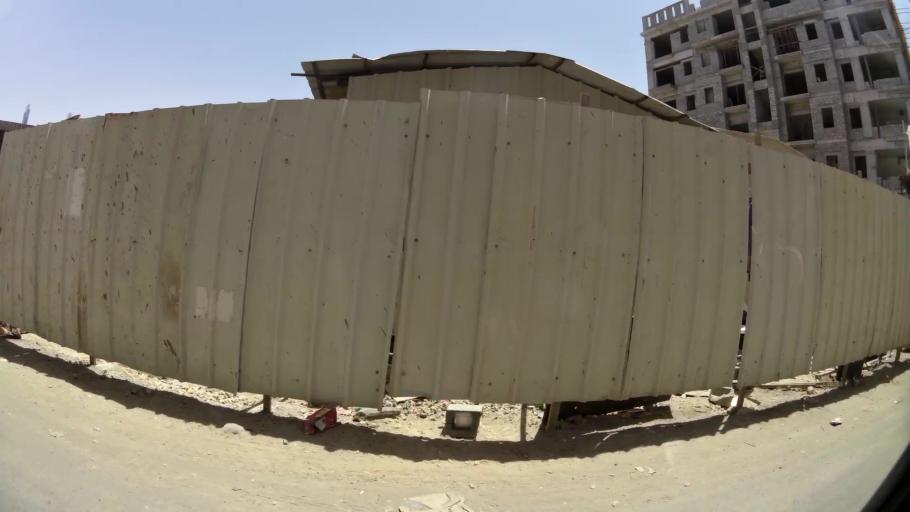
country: OM
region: Muhafazat Masqat
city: Muscat
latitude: 23.6240
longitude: 58.5034
